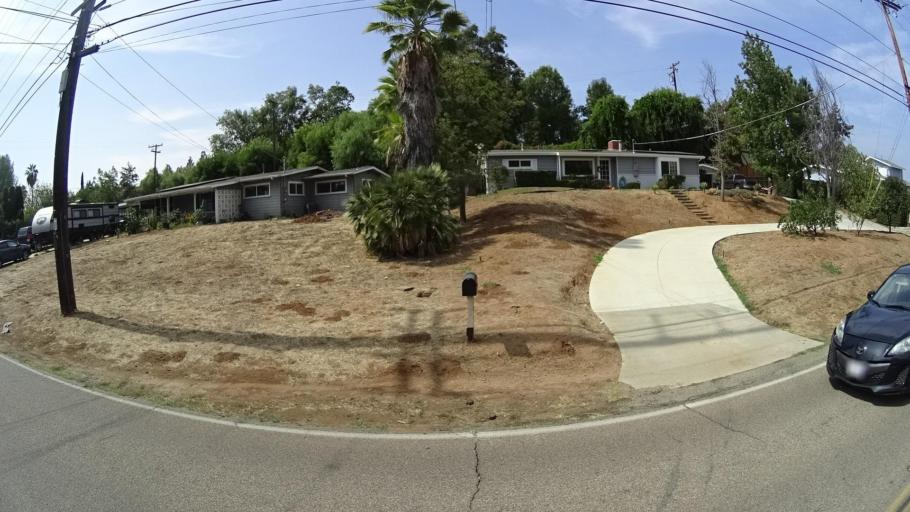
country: US
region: California
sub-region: San Diego County
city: Escondido
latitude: 33.1238
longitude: -117.0398
